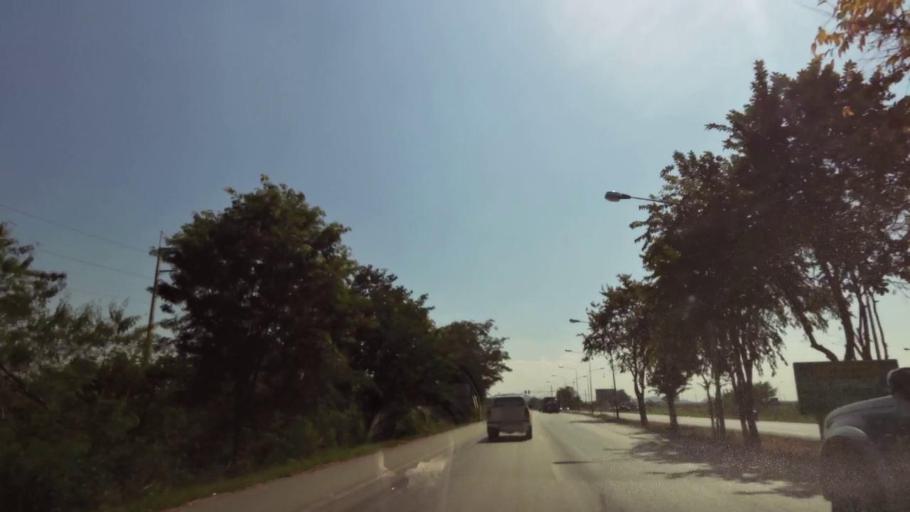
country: TH
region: Nakhon Sawan
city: Nakhon Sawan
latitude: 15.7698
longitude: 100.1214
